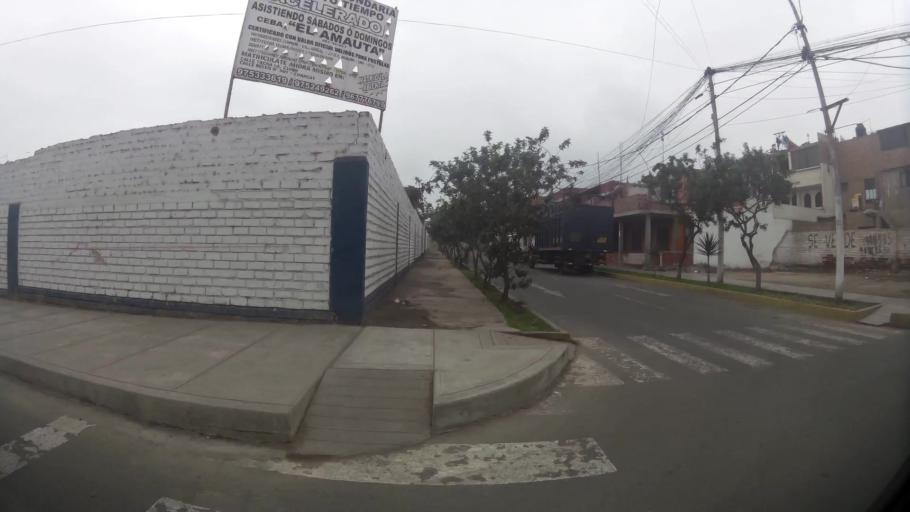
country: PE
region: Lima
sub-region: Provincia de Huaral
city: Chancay
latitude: -11.5691
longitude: -77.2701
